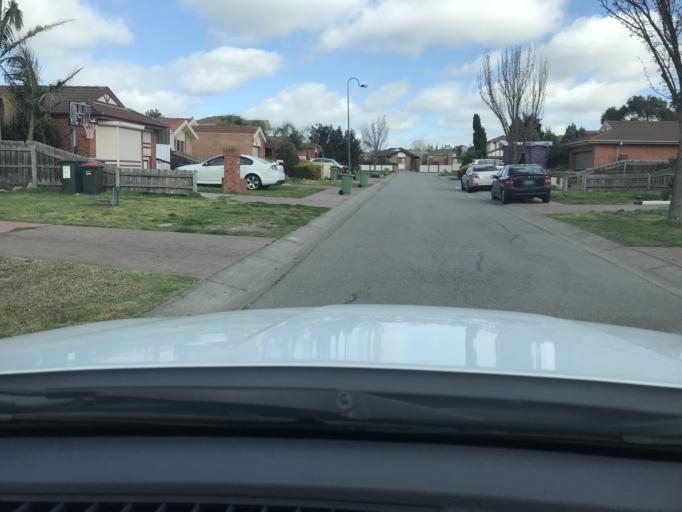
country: AU
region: Victoria
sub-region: Hume
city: Roxburgh Park
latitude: -37.6091
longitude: 144.9247
